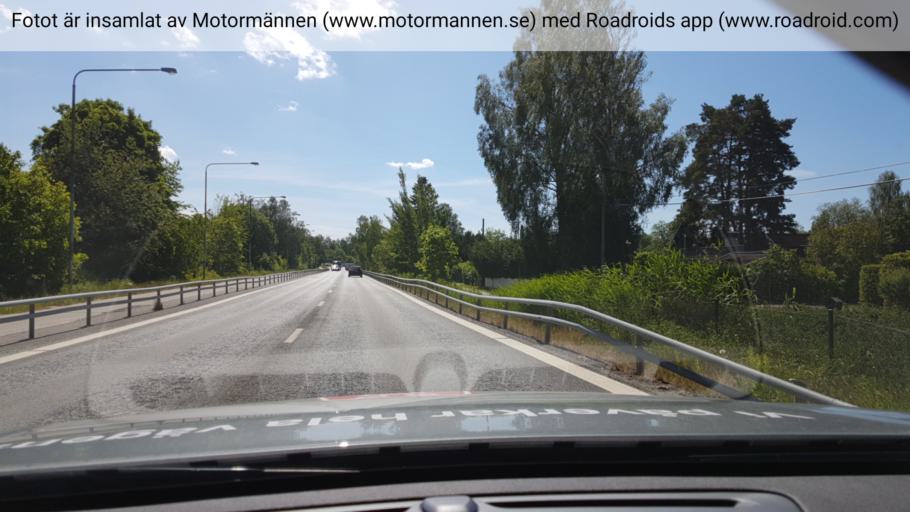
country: SE
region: Stockholm
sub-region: Tyreso Kommun
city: Bollmora
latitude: 59.2175
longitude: 18.2043
